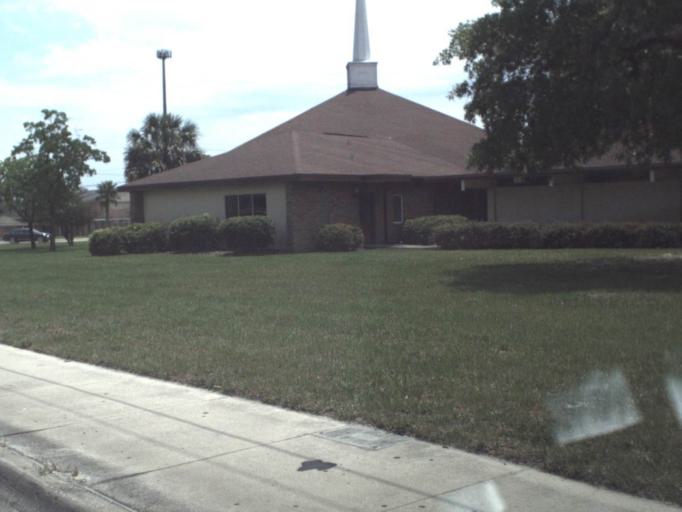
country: US
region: Florida
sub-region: Clay County
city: Lakeside
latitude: 30.1374
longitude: -81.7748
